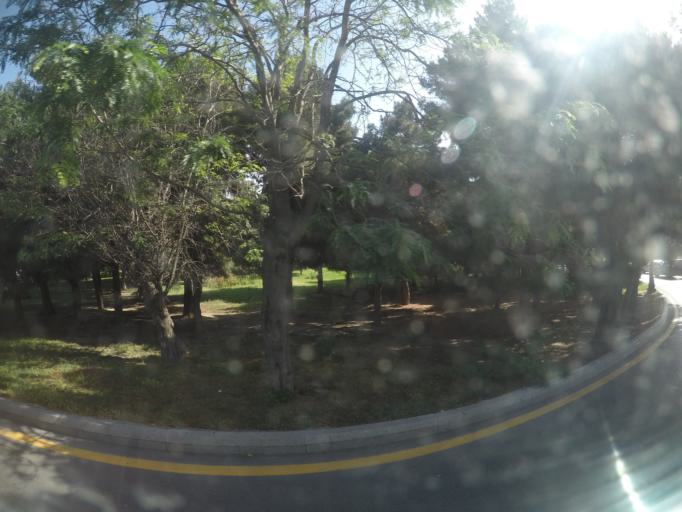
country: AZ
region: Baki
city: Badamdar
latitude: 40.3866
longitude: 49.8281
